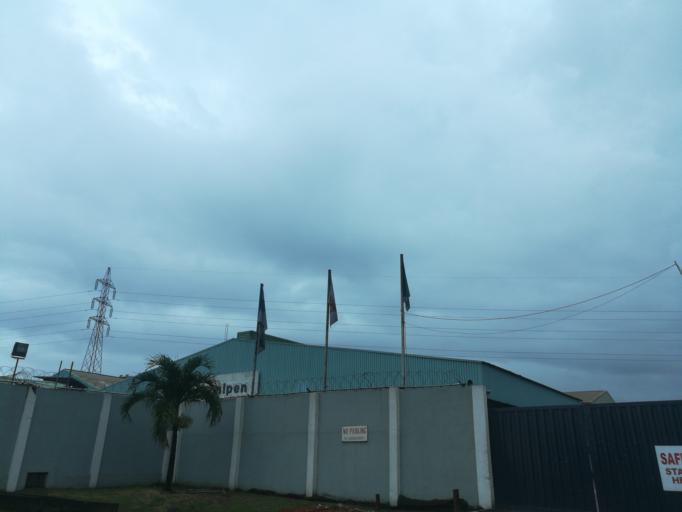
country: NG
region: Lagos
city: Agege
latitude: 6.6177
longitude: 3.3400
